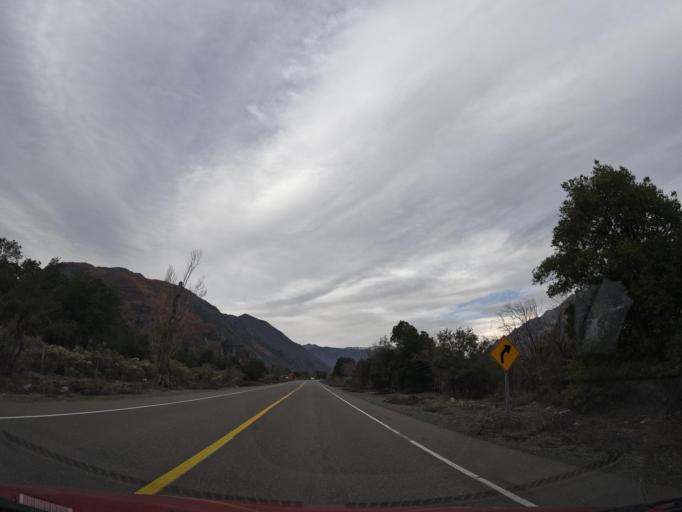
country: CL
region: Maule
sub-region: Provincia de Linares
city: Colbun
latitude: -35.7103
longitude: -71.0688
